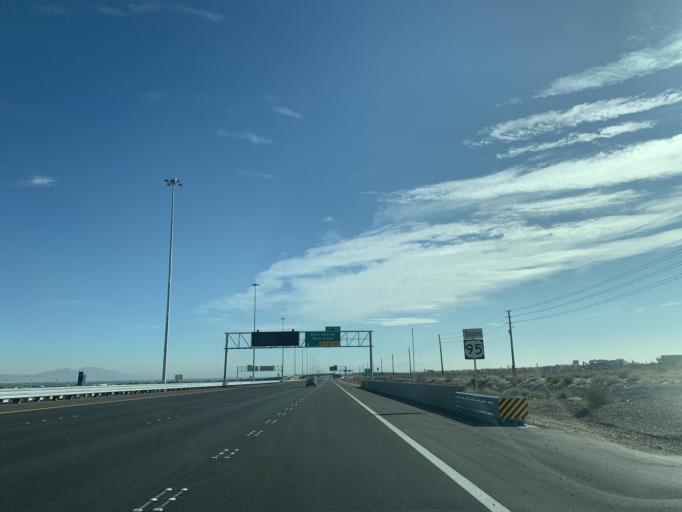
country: US
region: Nevada
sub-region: Clark County
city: Summerlin South
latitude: 36.3222
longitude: -115.3079
